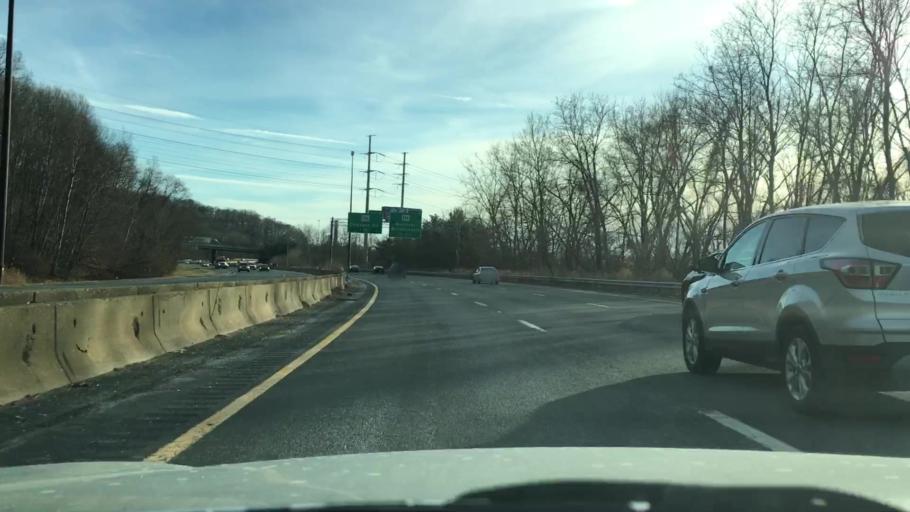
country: US
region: Massachusetts
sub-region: Hampden County
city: Chicopee
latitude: 42.1623
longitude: -72.6116
